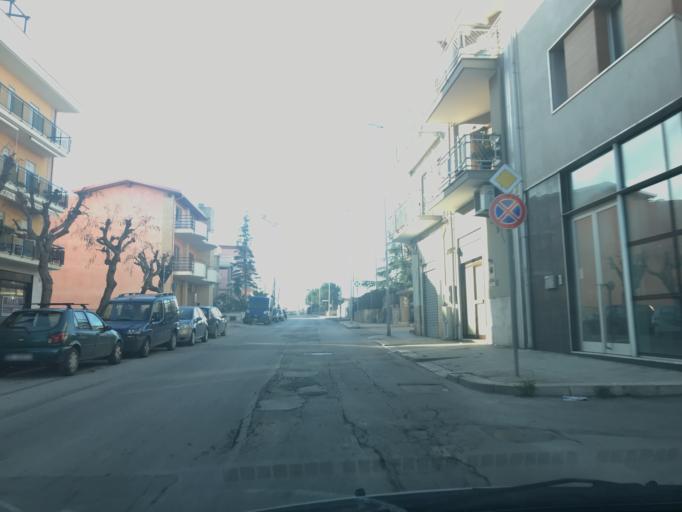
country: IT
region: Apulia
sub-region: Provincia di Bari
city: Corato
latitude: 41.1448
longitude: 16.4124
